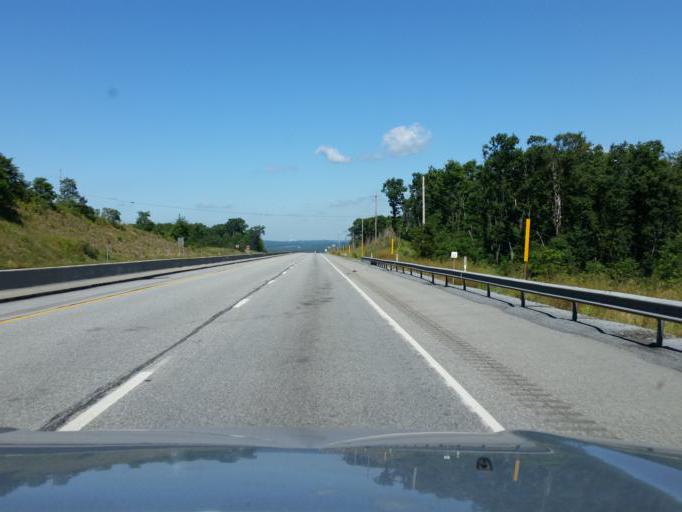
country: US
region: Pennsylvania
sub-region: Cambria County
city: Vinco
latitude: 40.4349
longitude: -78.9209
